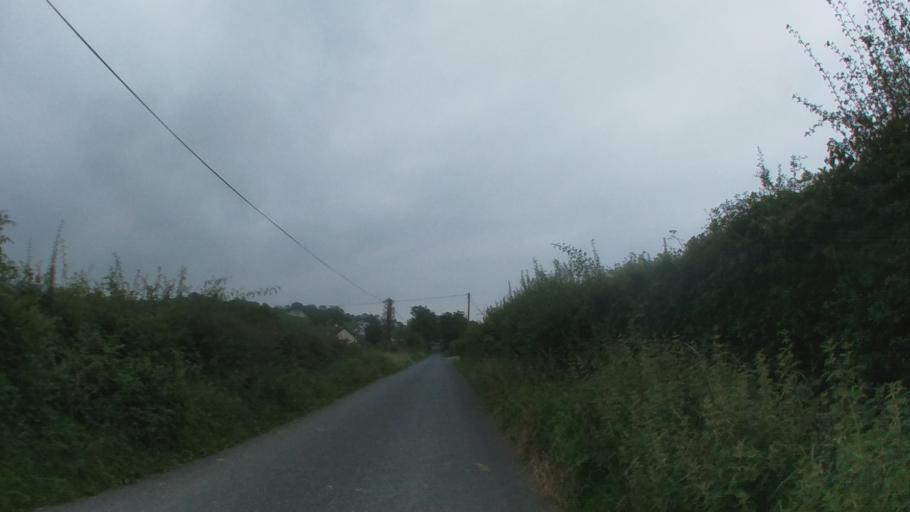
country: IE
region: Leinster
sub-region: Kilkenny
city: Kilkenny
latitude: 52.7060
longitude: -7.1931
